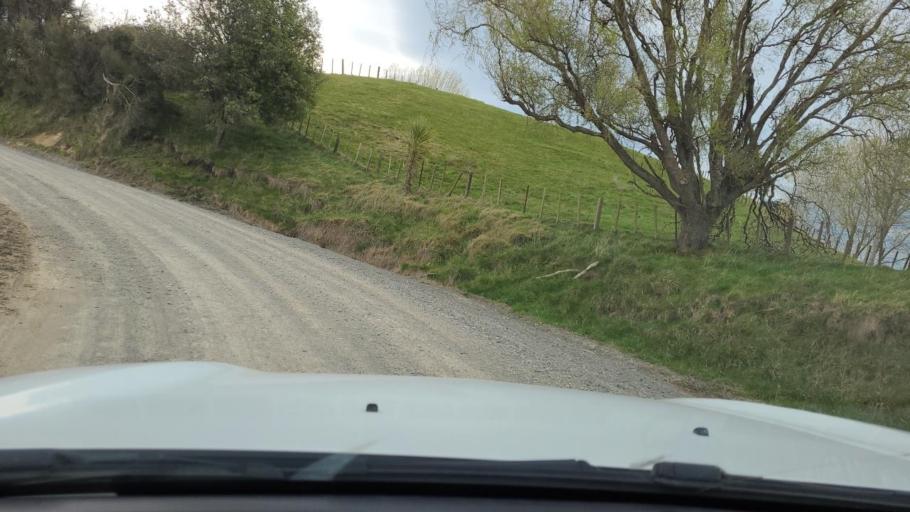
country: NZ
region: Hawke's Bay
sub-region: Napier City
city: Napier
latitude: -39.3453
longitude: 176.8302
